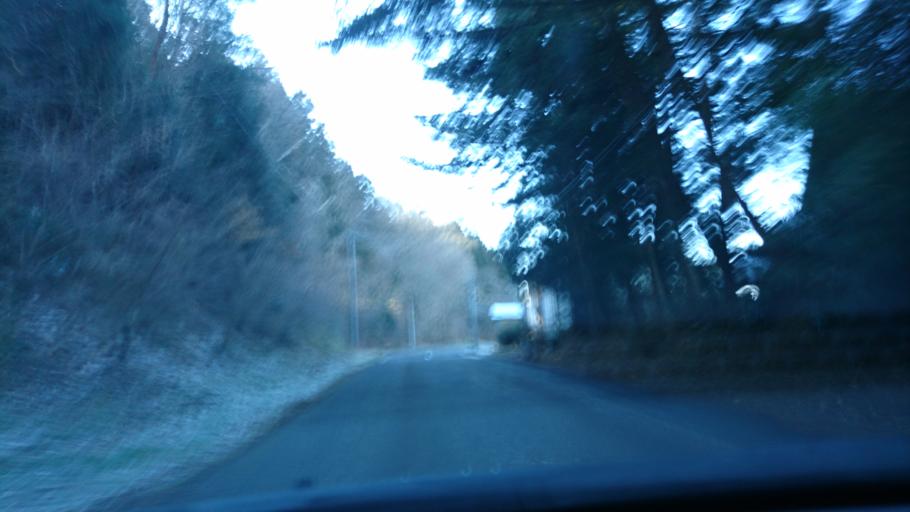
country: JP
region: Iwate
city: Ichinoseki
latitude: 38.8638
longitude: 141.2982
